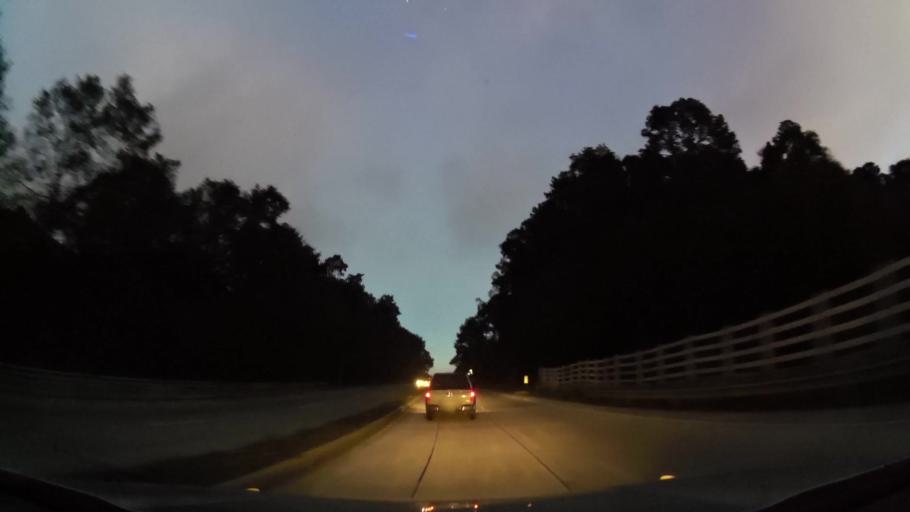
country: GT
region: Chimaltenango
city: Santa Apolonia
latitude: 14.7979
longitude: -90.9854
